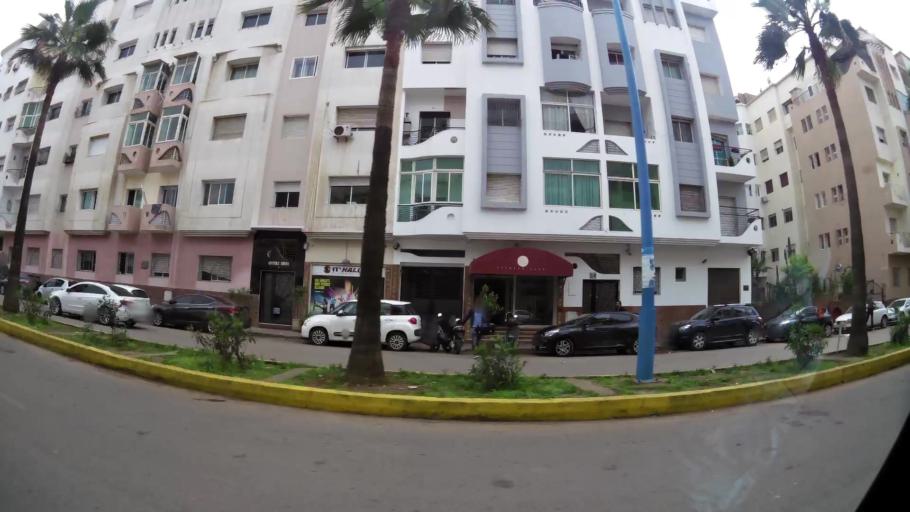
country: MA
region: Grand Casablanca
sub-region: Casablanca
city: Casablanca
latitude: 33.5991
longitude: -7.6465
